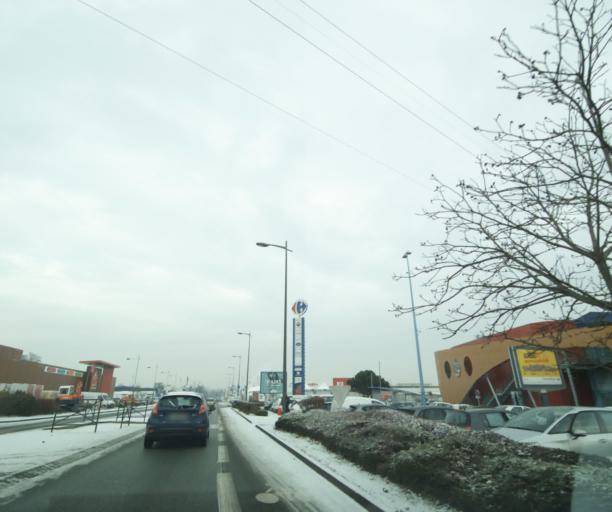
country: FR
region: Auvergne
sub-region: Departement du Puy-de-Dome
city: Menetrol
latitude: 45.8765
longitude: 3.1164
